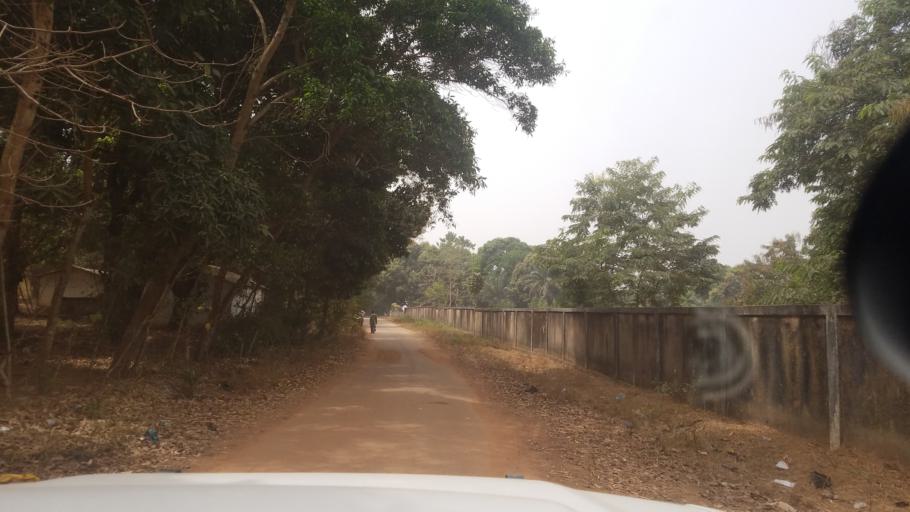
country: GN
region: Kindia
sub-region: Prefecture de Dubreka
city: Dubreka
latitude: 9.7869
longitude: -13.5124
